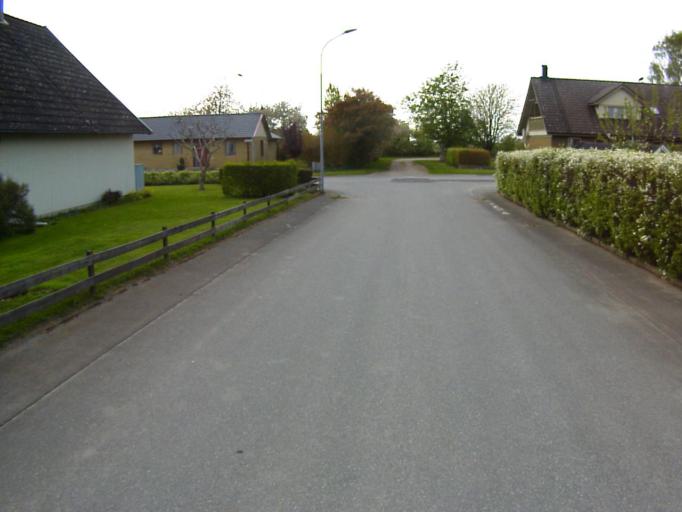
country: SE
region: Skane
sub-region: Kristianstads Kommun
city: Fjalkinge
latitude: 56.0479
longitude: 14.2756
